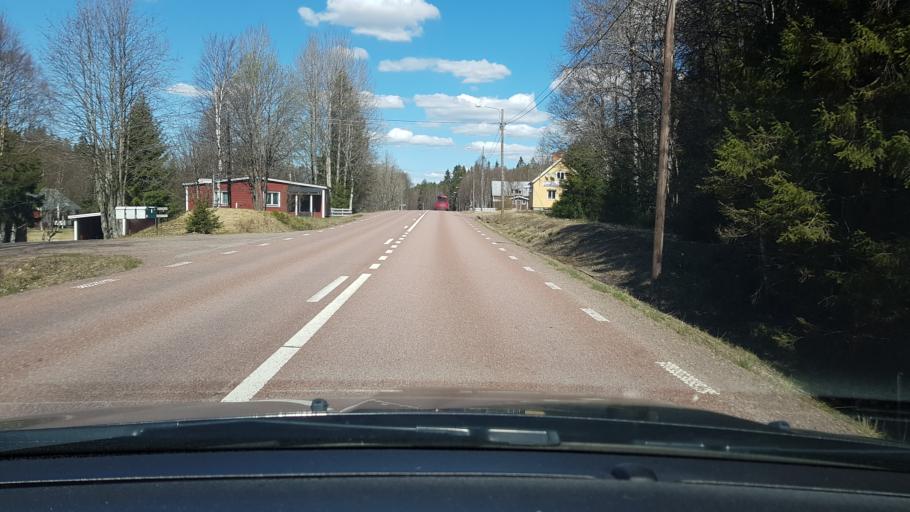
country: SE
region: Dalarna
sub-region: Malung-Saelens kommun
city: Malung
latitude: 61.0718
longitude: 13.3294
